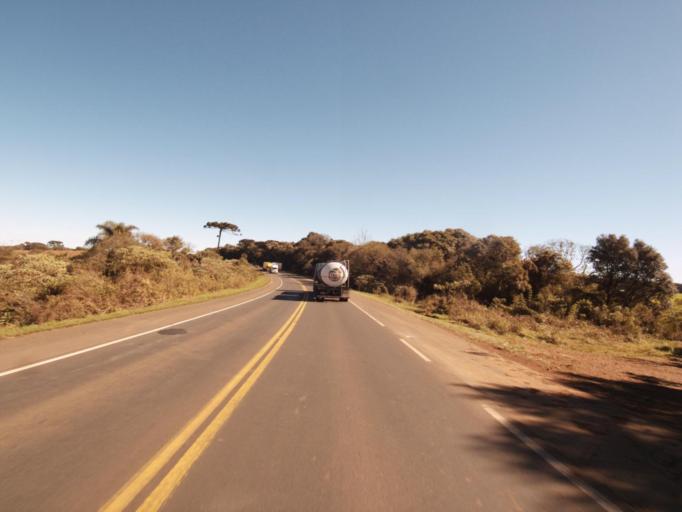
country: BR
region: Santa Catarina
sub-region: Xanxere
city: Xanxere
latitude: -26.8694
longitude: -52.3152
